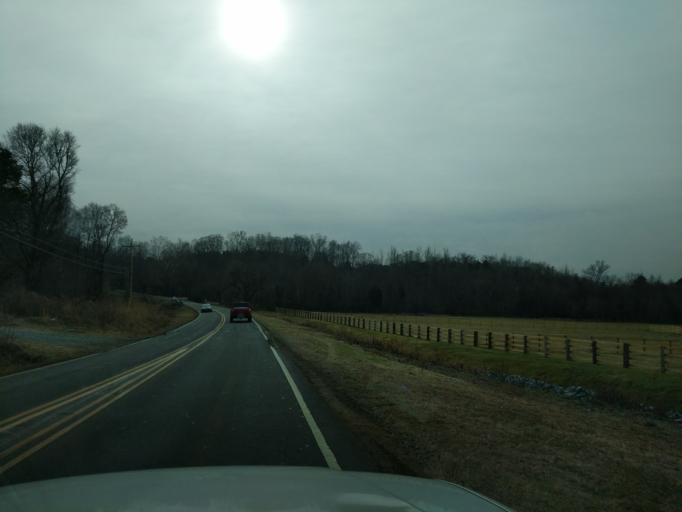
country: US
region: North Carolina
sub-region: Mecklenburg County
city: Huntersville
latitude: 35.3298
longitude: -80.9108
